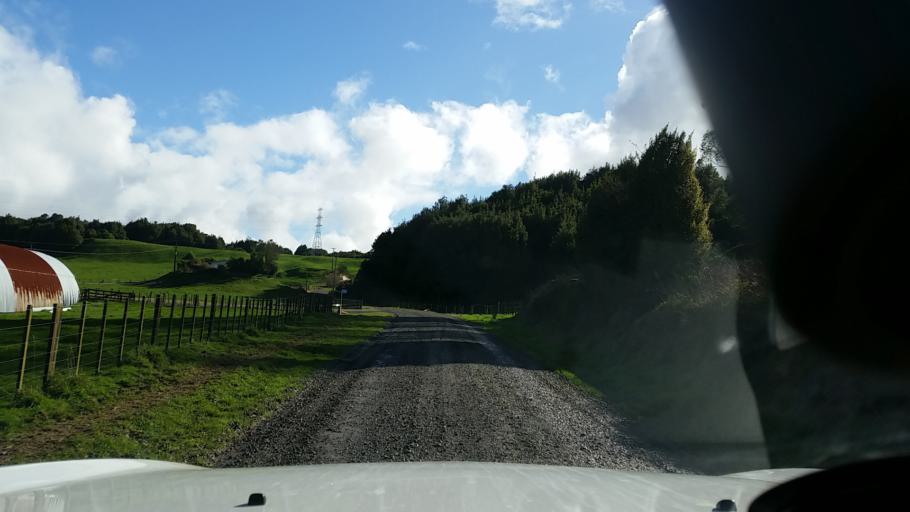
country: NZ
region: Bay of Plenty
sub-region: Rotorua District
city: Rotorua
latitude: -37.9913
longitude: 176.1805
